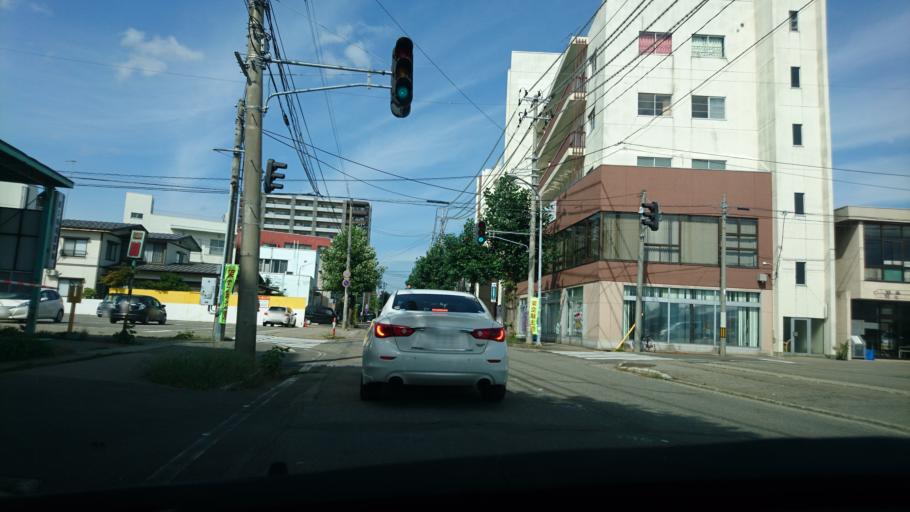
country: JP
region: Akita
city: Yokotemachi
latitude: 39.3095
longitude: 140.5626
